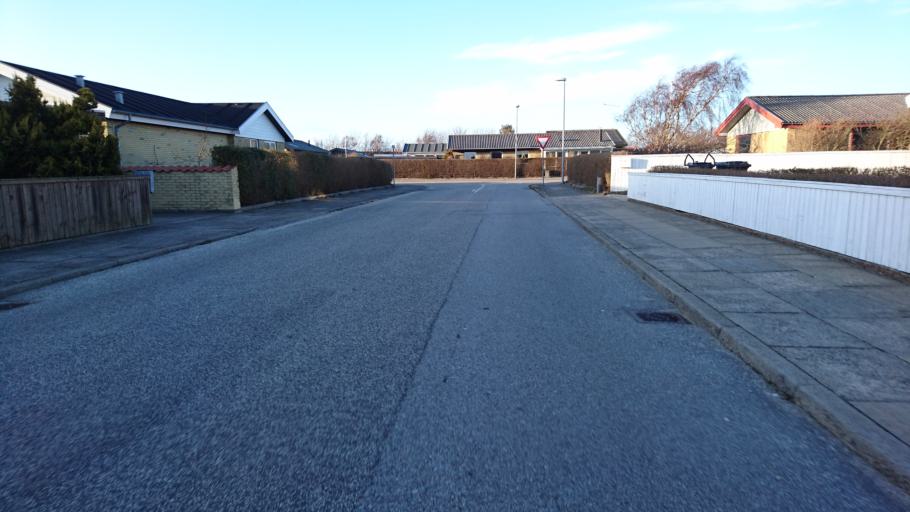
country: DK
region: North Denmark
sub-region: Frederikshavn Kommune
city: Skagen
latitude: 57.7302
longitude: 10.5915
